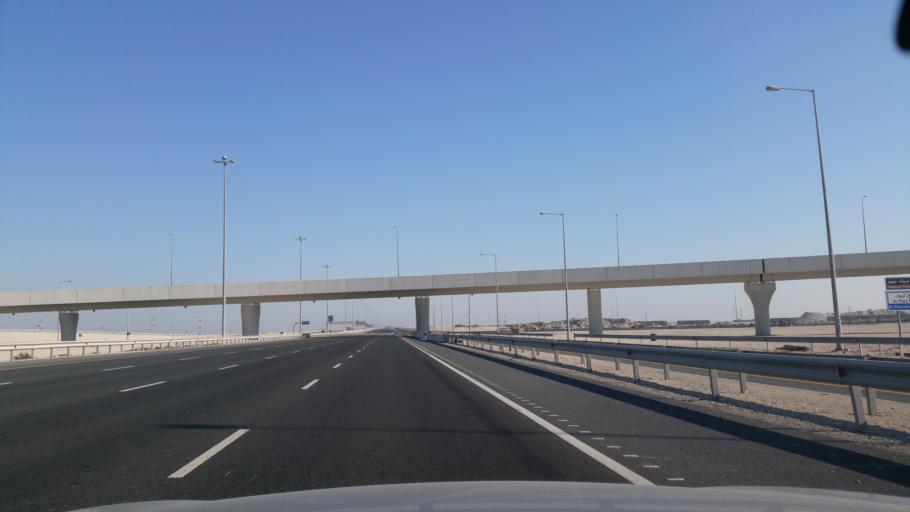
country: QA
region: Al Wakrah
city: Al Wukayr
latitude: 25.1214
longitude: 51.4881
